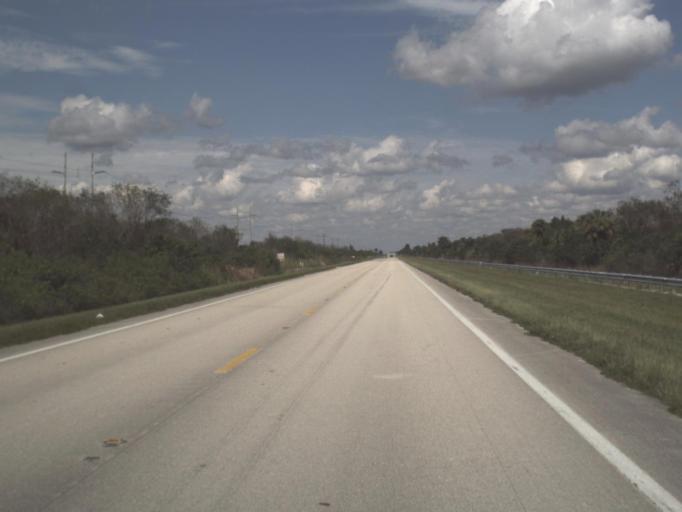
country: US
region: Florida
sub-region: Collier County
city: Orangetree
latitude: 26.1283
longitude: -81.3449
